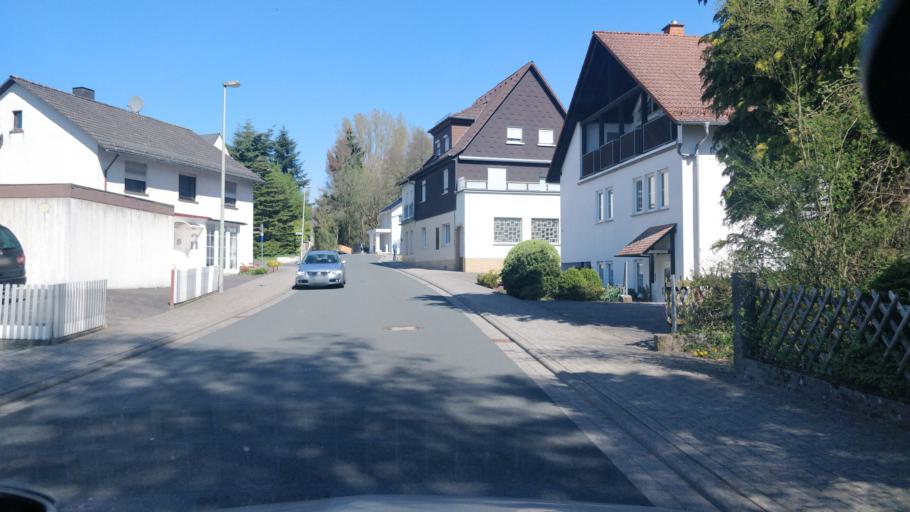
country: DE
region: Hesse
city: Waldbrunn
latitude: 50.5268
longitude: 8.0963
